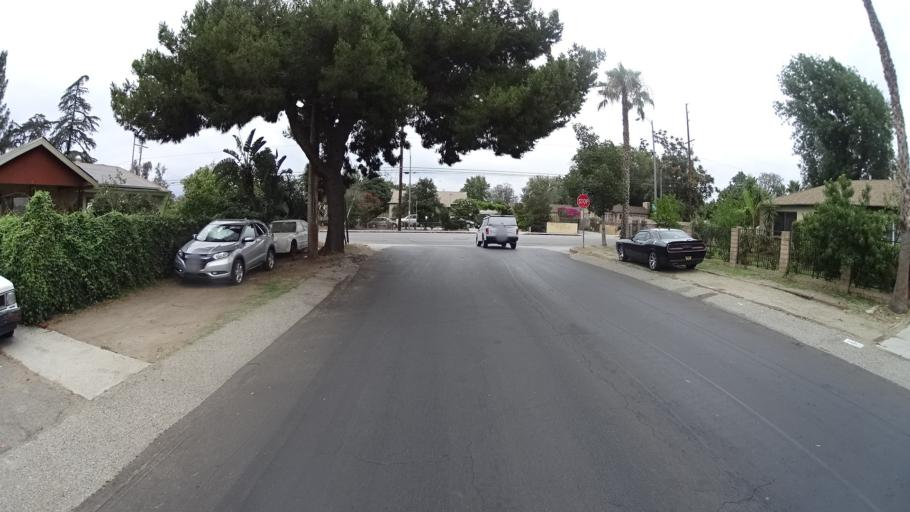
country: US
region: California
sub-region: Los Angeles County
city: San Fernando
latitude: 34.2424
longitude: -118.4537
